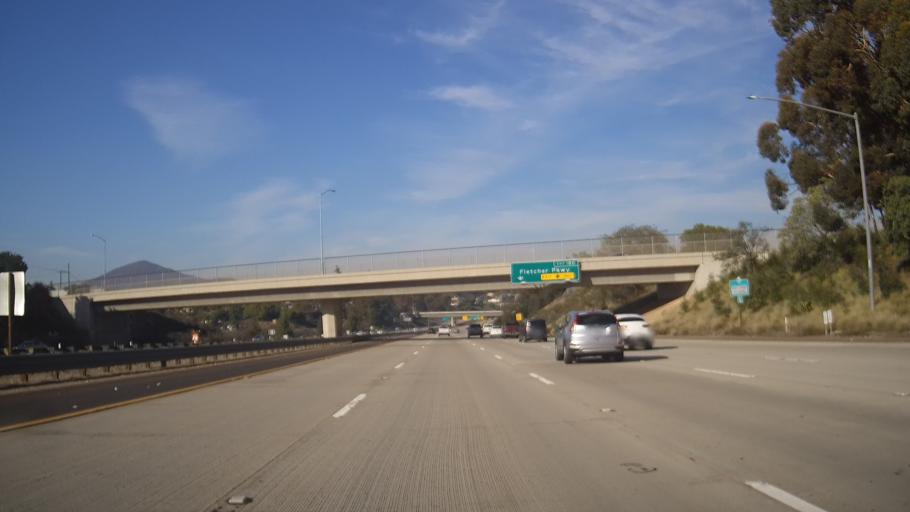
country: US
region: California
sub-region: San Diego County
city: La Mesa
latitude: 32.7814
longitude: -117.0047
